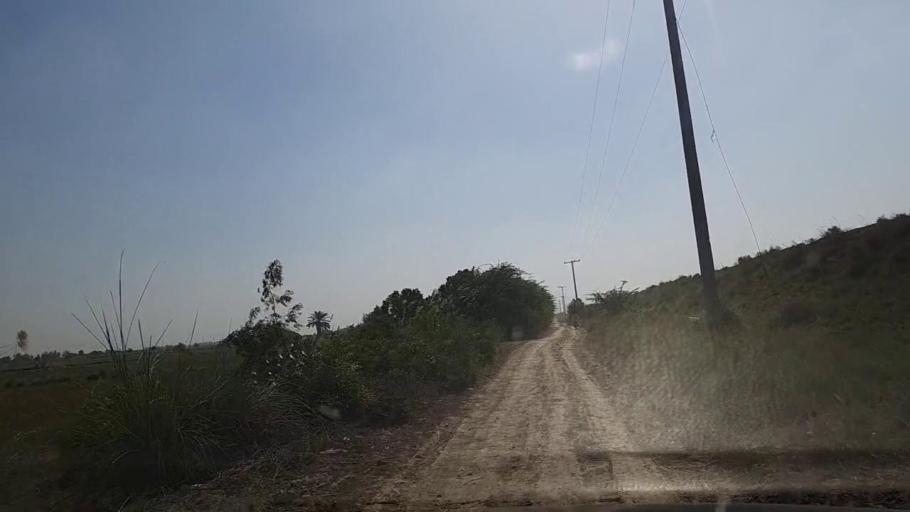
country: PK
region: Sindh
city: Daro Mehar
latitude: 24.7796
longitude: 68.0701
